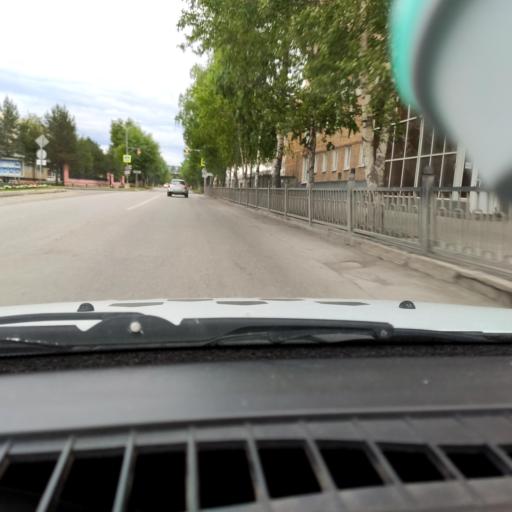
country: RU
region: Perm
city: Chusovoy
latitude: 58.2952
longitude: 57.8132
